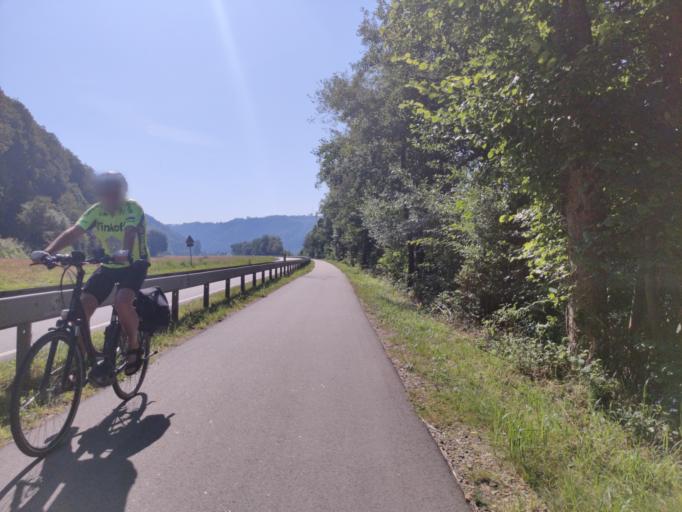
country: DE
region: Bavaria
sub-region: Lower Bavaria
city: Thyrnau
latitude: 48.5709
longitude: 13.5525
